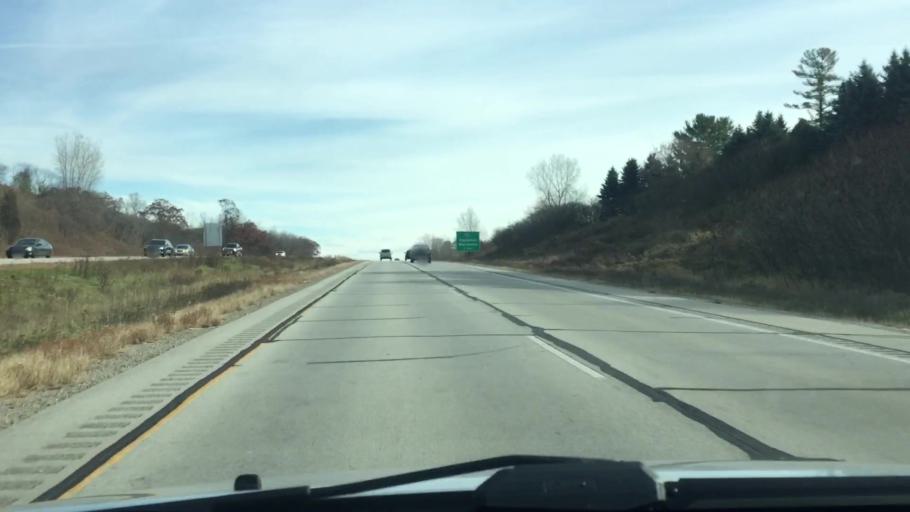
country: US
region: Wisconsin
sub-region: Brown County
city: Howard
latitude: 44.5526
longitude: -88.1115
